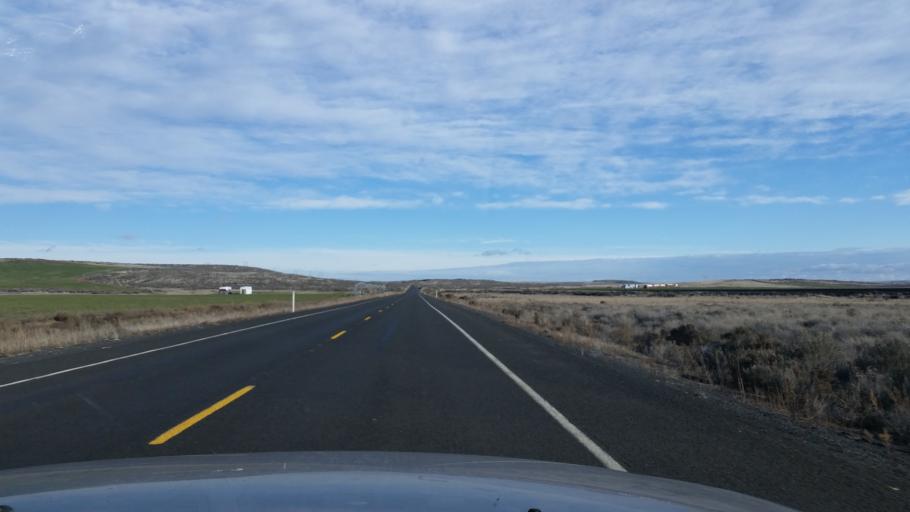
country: US
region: Washington
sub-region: Adams County
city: Ritzville
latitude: 47.3382
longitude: -118.6358
